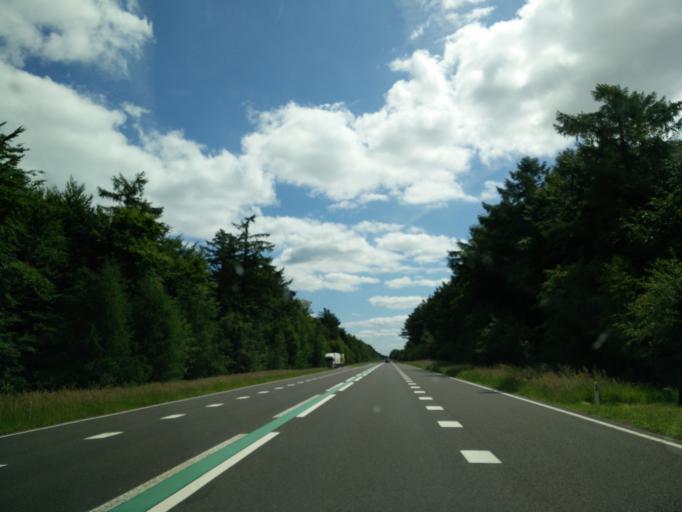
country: NL
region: Drenthe
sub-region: Gemeente Coevorden
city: Sleen
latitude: 52.8003
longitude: 6.7628
